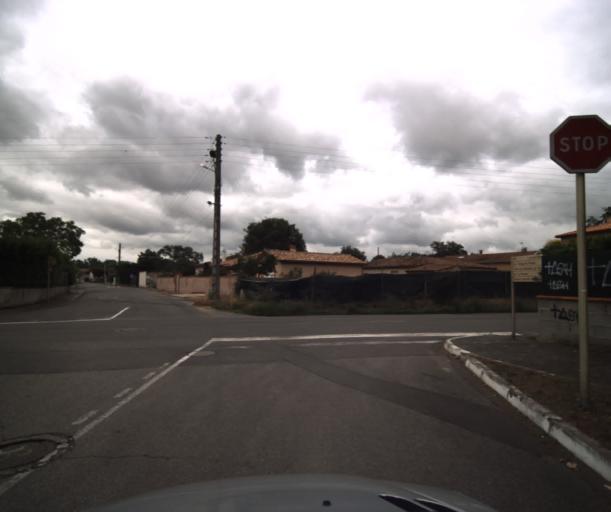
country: FR
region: Midi-Pyrenees
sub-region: Departement de la Haute-Garonne
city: Pinsaguel
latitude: 43.4986
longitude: 1.3938
